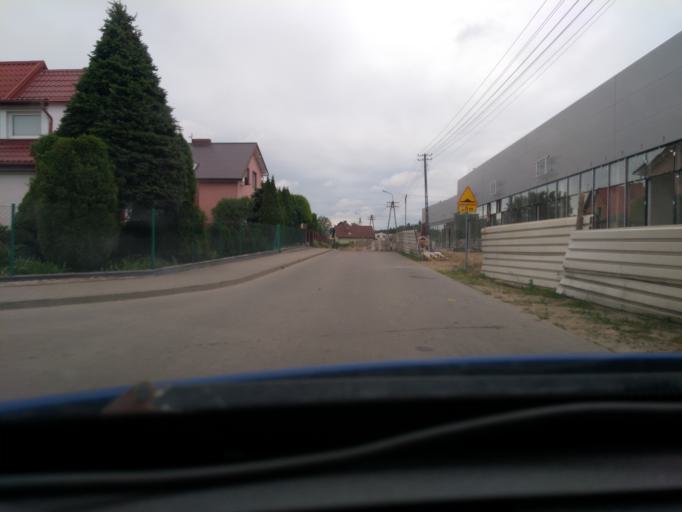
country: PL
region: Pomeranian Voivodeship
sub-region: Powiat kartuski
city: Banino
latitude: 54.3944
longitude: 18.4044
